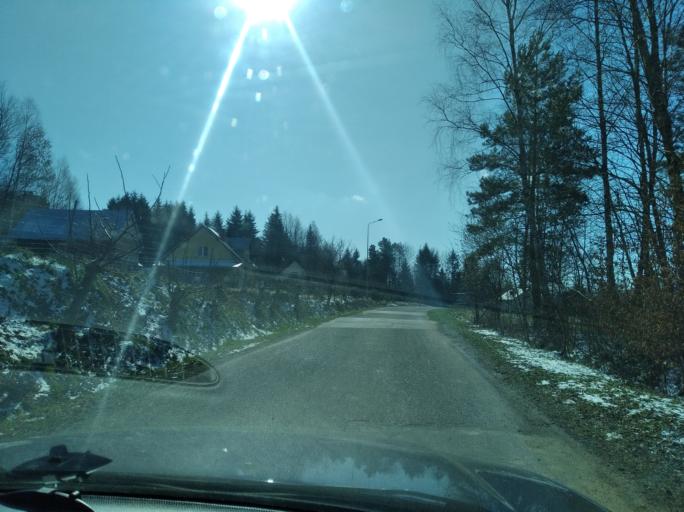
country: PL
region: Subcarpathian Voivodeship
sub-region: Powiat strzyzowski
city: Jawornik
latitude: 49.8566
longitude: 21.8679
